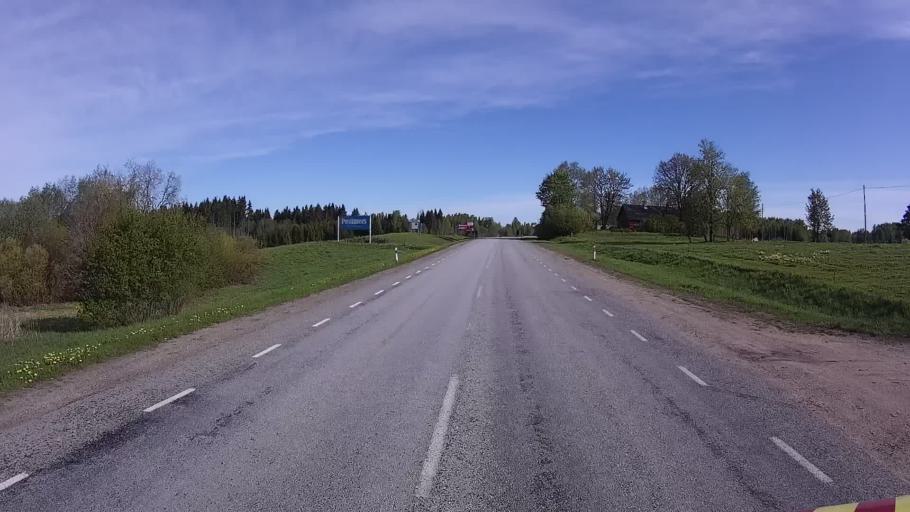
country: EE
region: Tartu
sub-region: Elva linn
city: Elva
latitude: 58.0690
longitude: 26.4993
